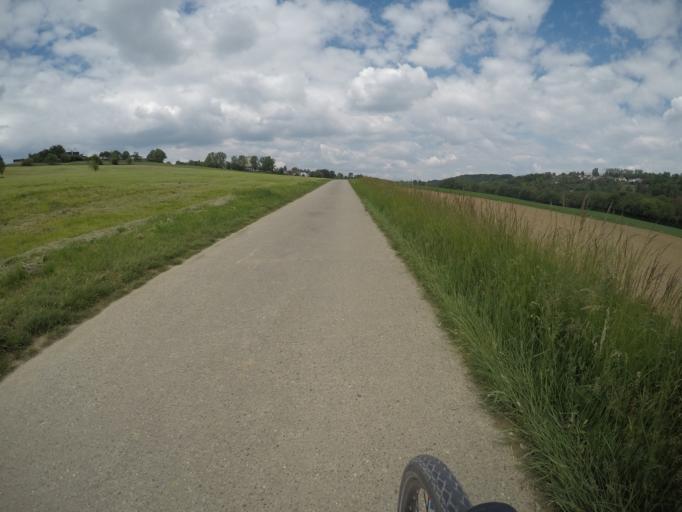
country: DE
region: Baden-Wuerttemberg
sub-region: Regierungsbezirk Stuttgart
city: Ostfildern
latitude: 48.7144
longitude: 9.2213
